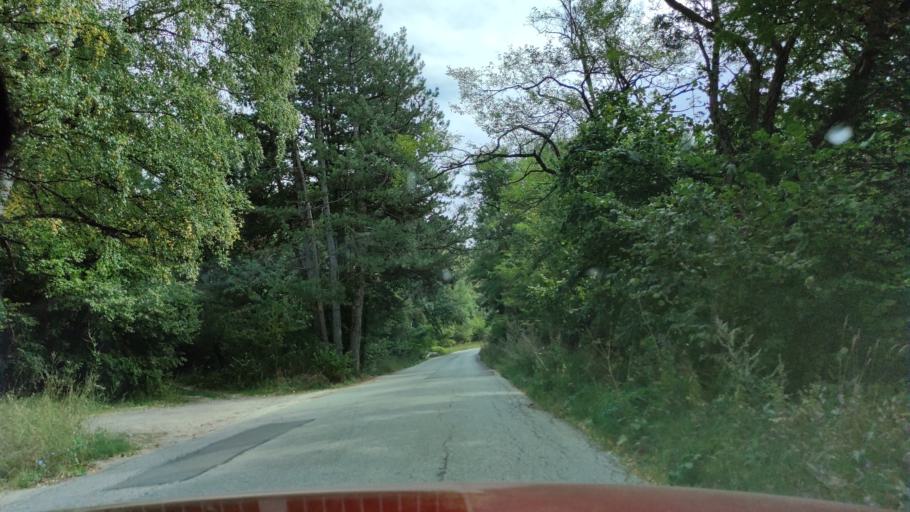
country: BG
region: Sofia-Capital
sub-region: Stolichna Obshtina
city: Sofia
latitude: 42.6207
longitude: 23.2257
